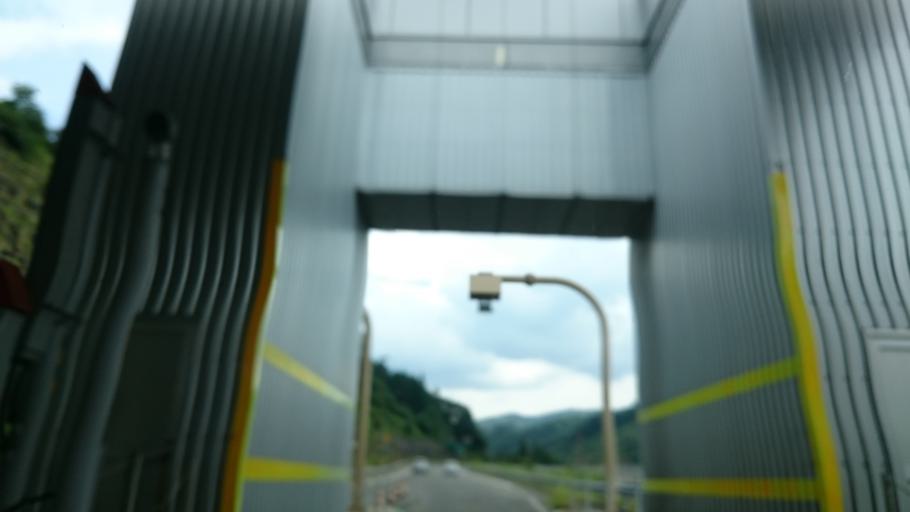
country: JP
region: Gifu
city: Takayama
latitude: 36.1344
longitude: 137.0776
